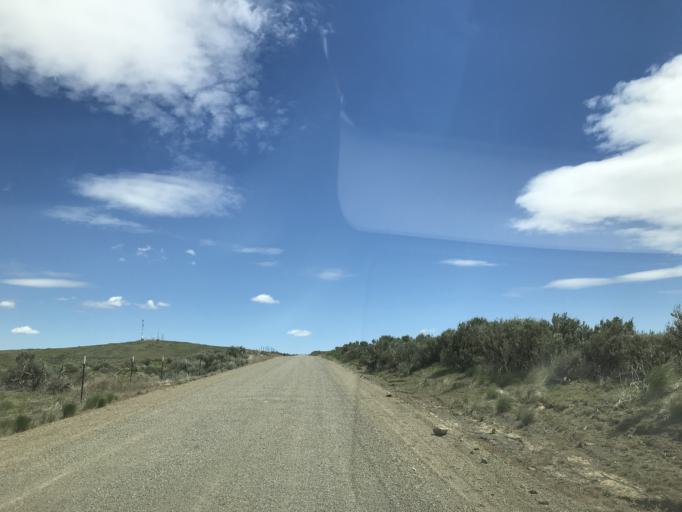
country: US
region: Washington
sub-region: Grant County
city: Quincy
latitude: 47.3170
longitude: -119.8165
